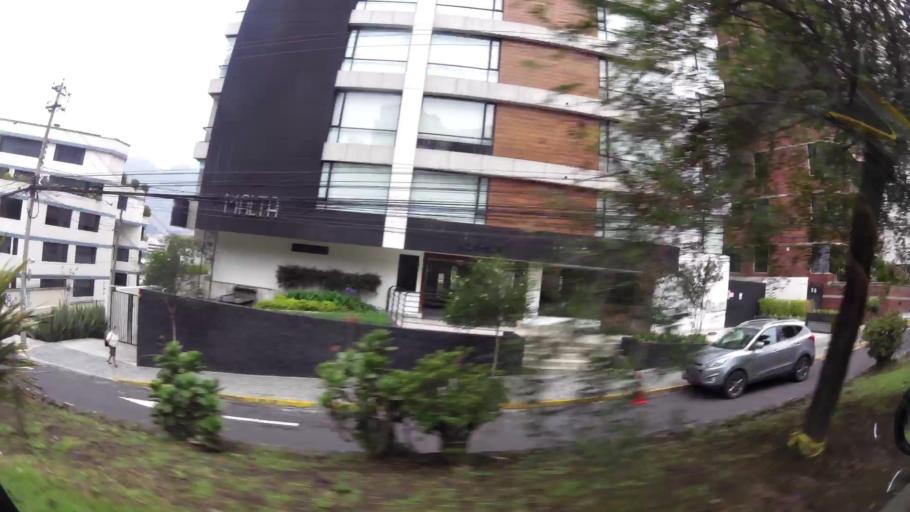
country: EC
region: Pichincha
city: Quito
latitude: -0.1954
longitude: -78.4800
